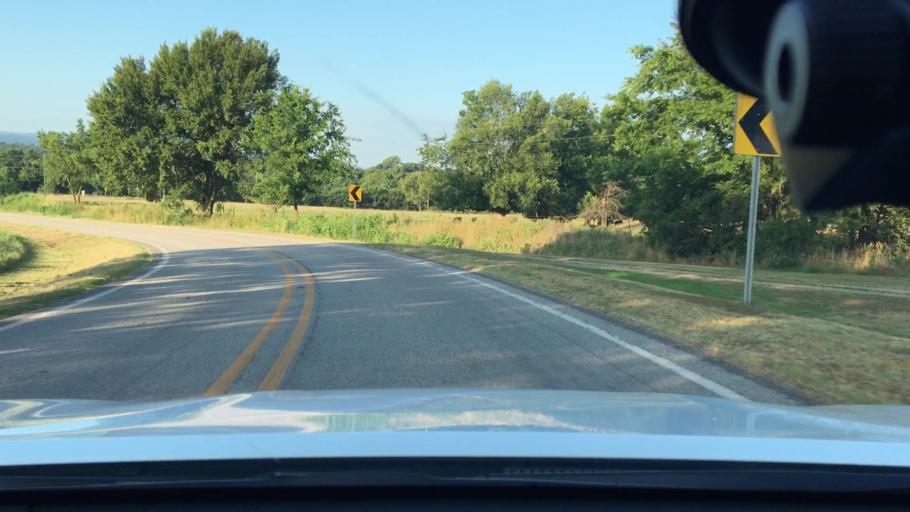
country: US
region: Arkansas
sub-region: Johnson County
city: Coal Hill
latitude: 35.3393
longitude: -93.6037
